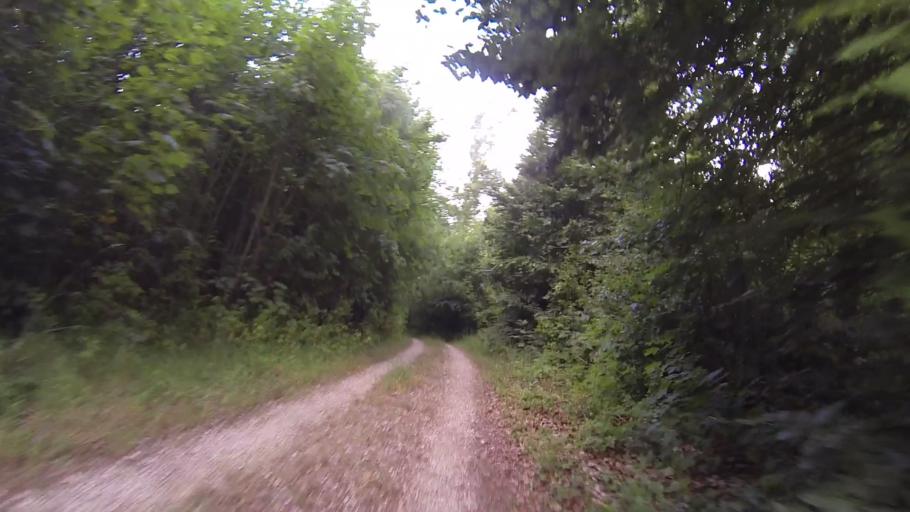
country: DE
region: Baden-Wuerttemberg
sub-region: Tuebingen Region
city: Dornstadt
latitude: 48.4349
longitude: 9.8762
